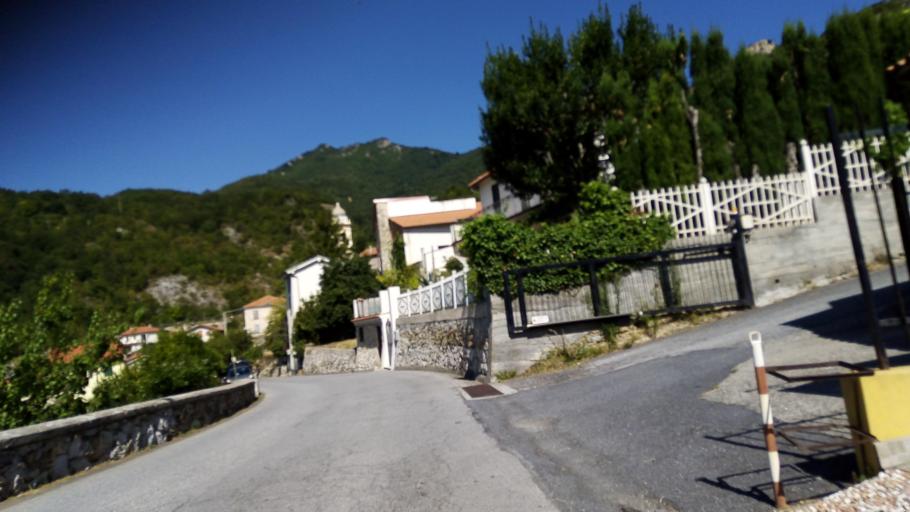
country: IT
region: Liguria
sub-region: Provincia di Savona
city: Balestrino
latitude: 44.1424
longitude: 8.1652
